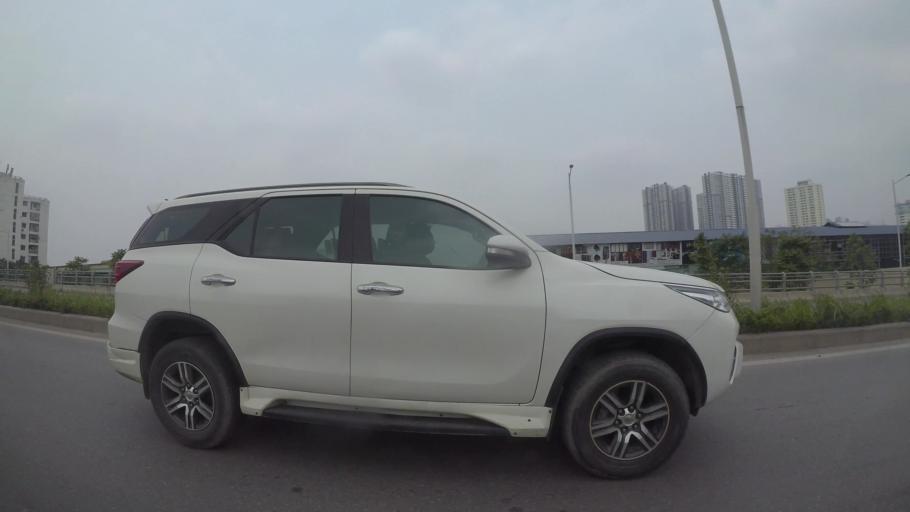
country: VN
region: Ha Noi
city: Cau Dien
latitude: 21.0333
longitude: 105.7543
